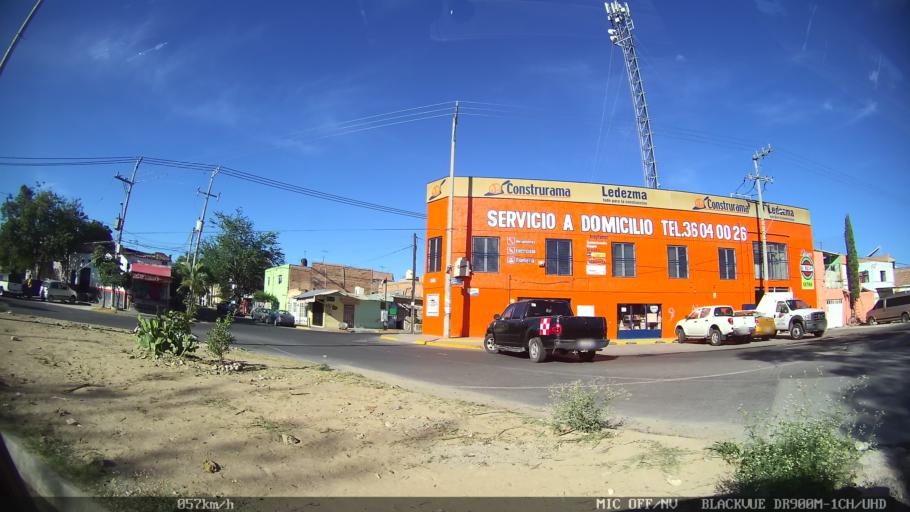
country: MX
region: Jalisco
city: Tlaquepaque
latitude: 20.6974
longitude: -103.2752
